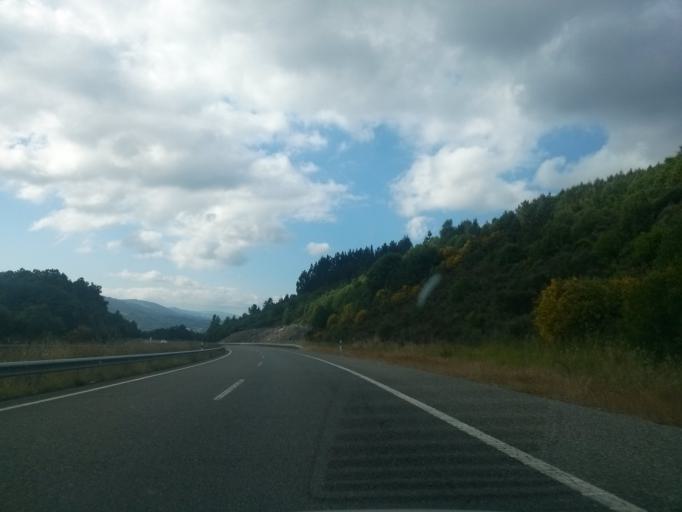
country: ES
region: Galicia
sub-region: Provincia de Lugo
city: Becerrea
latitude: 42.8931
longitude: -7.1842
